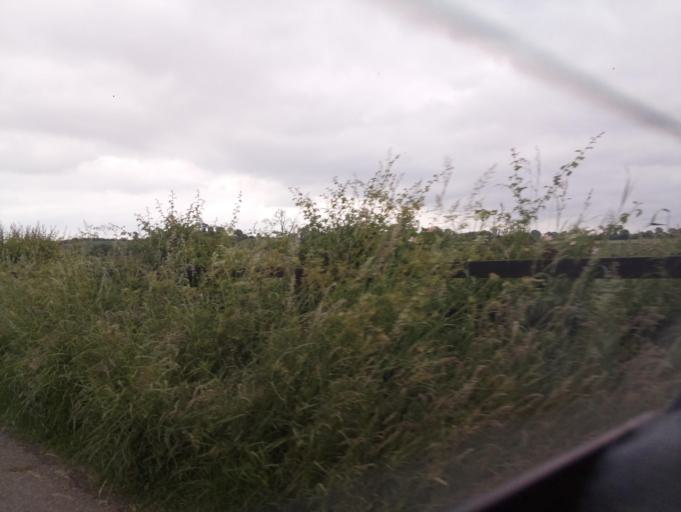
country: GB
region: England
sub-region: District of Rutland
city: Langham
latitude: 52.6839
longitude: -0.8341
